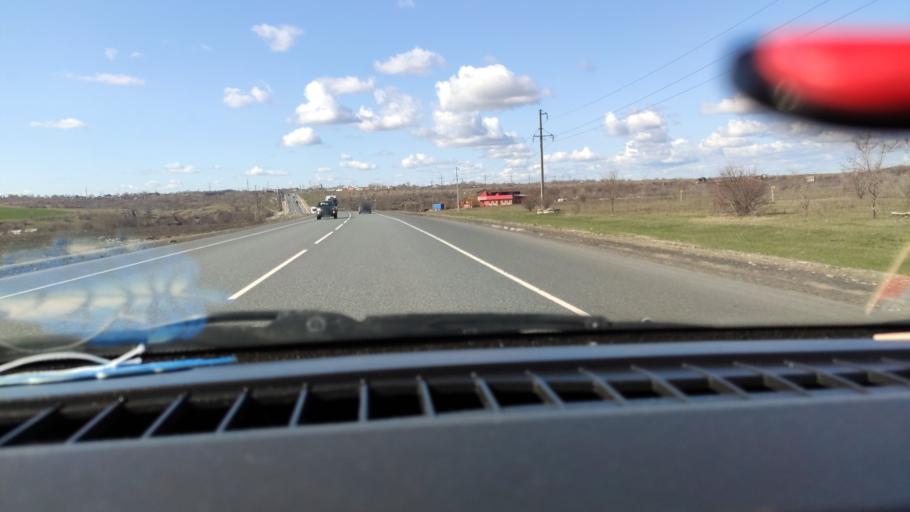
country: RU
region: Samara
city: Varlamovo
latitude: 53.2044
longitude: 48.3823
